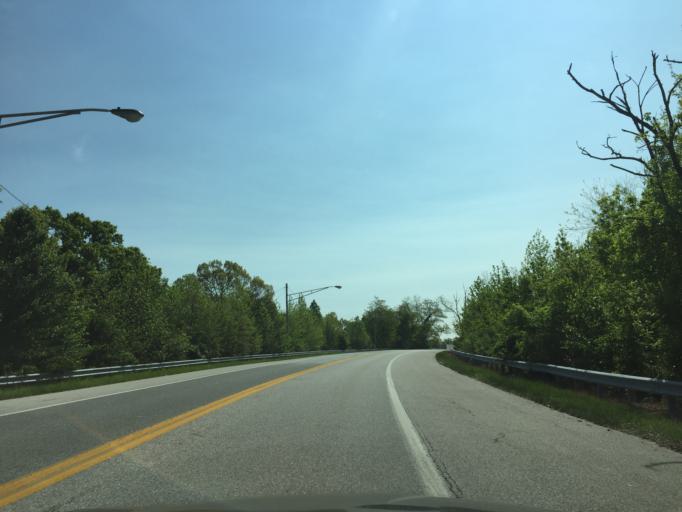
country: US
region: Maryland
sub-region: Baltimore County
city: Bowleys Quarters
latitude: 39.3645
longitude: -76.3697
